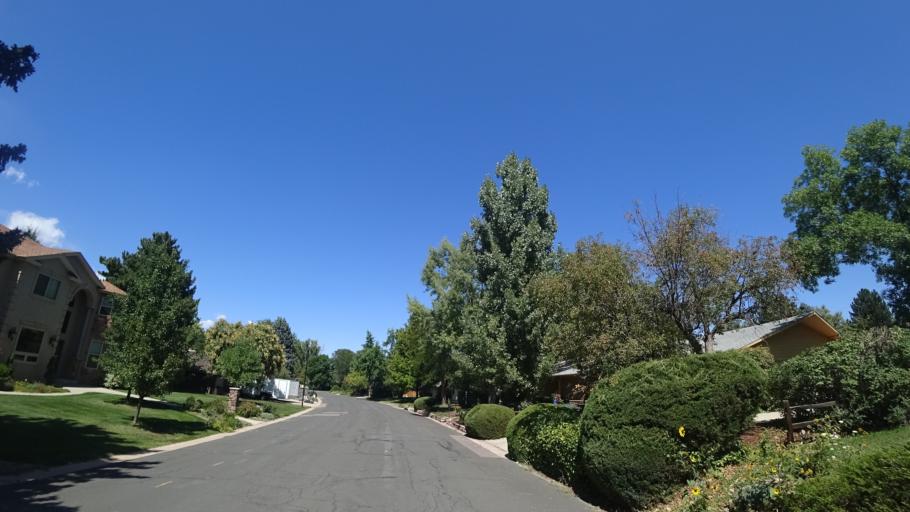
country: US
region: Colorado
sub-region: Arapahoe County
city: Littleton
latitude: 39.6067
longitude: -104.9956
